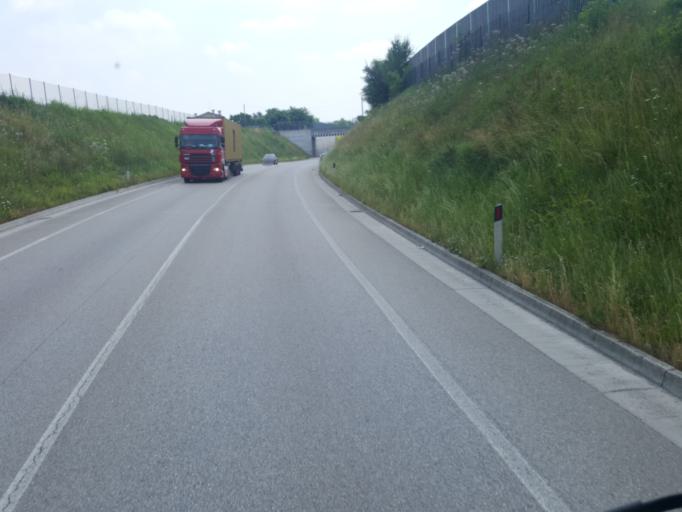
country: IT
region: Veneto
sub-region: Provincia di Treviso
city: Lancenigo-Villorba
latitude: 45.7409
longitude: 12.2723
